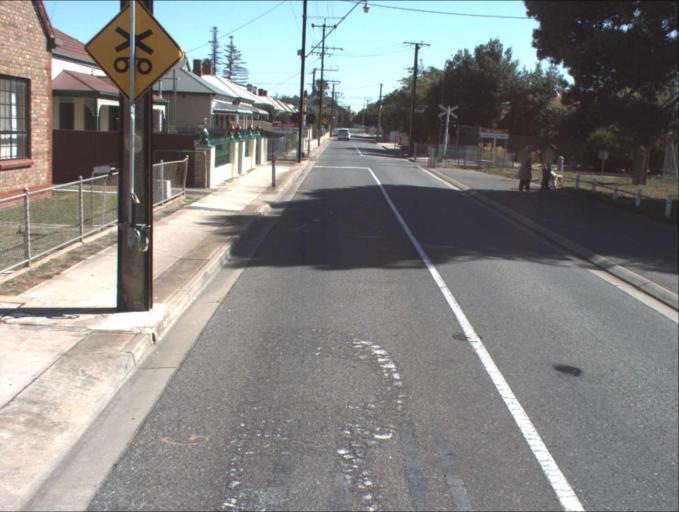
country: AU
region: South Australia
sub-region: Port Adelaide Enfield
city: Alberton
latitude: -34.8542
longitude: 138.5192
